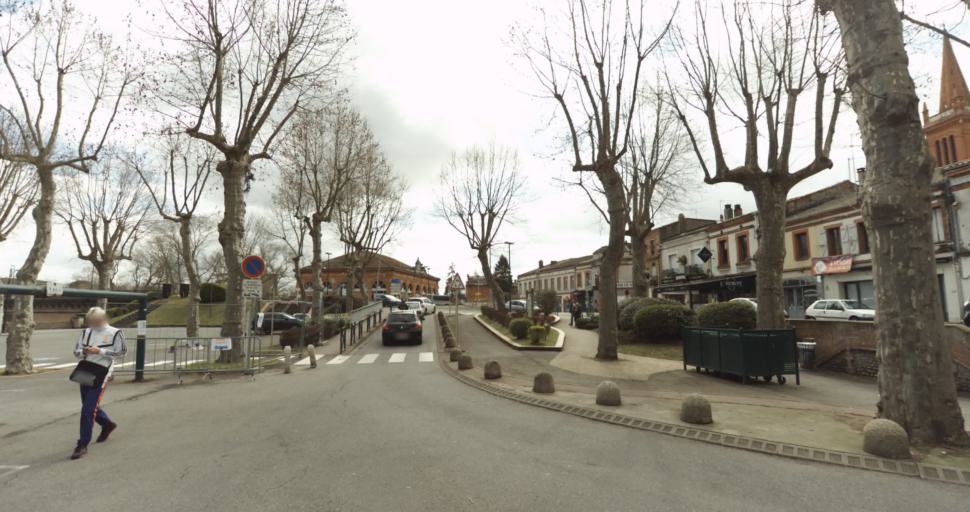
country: FR
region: Midi-Pyrenees
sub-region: Departement de la Haute-Garonne
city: Auterive
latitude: 43.3511
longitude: 1.4738
